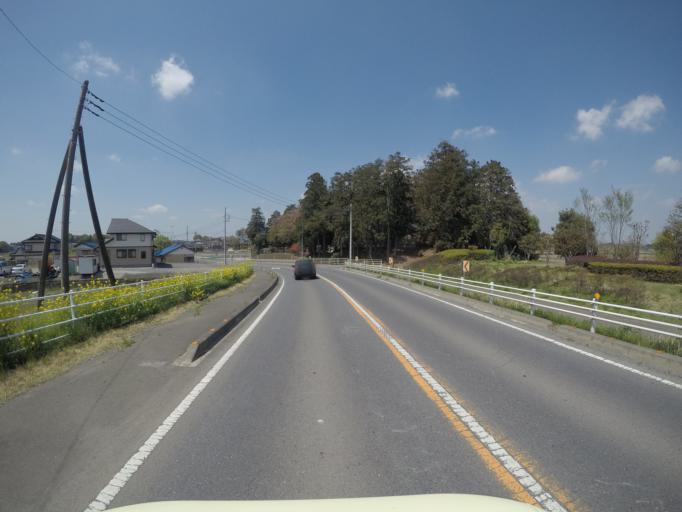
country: JP
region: Tochigi
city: Mibu
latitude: 36.3898
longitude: 139.8278
